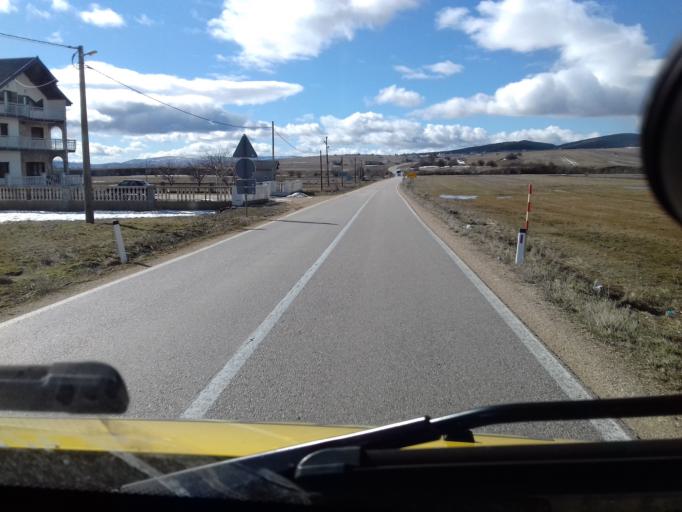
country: BA
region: Federation of Bosnia and Herzegovina
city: Tomislavgrad
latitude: 43.7603
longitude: 17.2347
